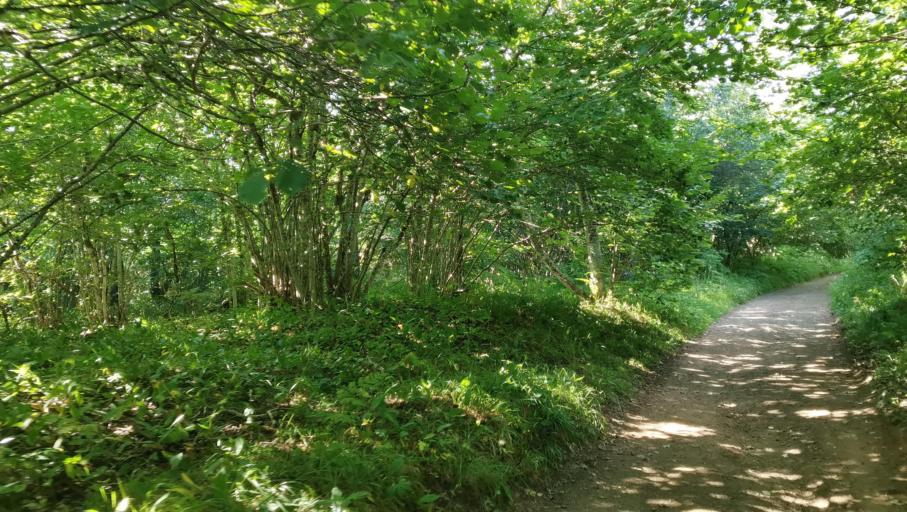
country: FR
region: Auvergne
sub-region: Departement du Puy-de-Dome
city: Orcines
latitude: 45.7996
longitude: 2.9648
